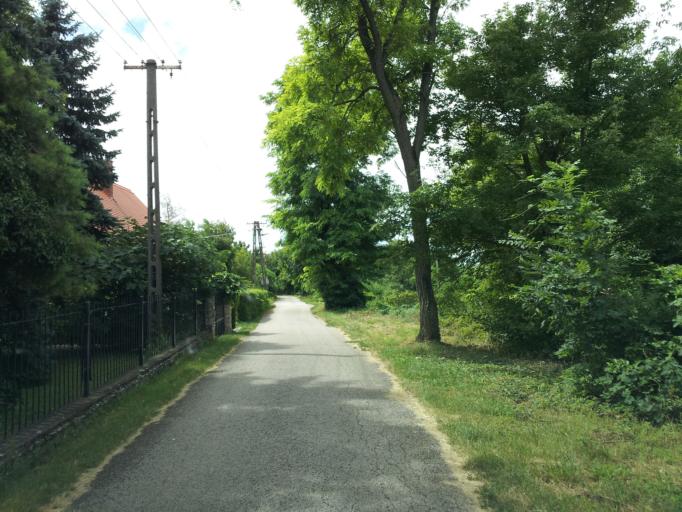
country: HU
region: Fejer
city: Lepseny
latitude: 46.9911
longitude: 18.1699
